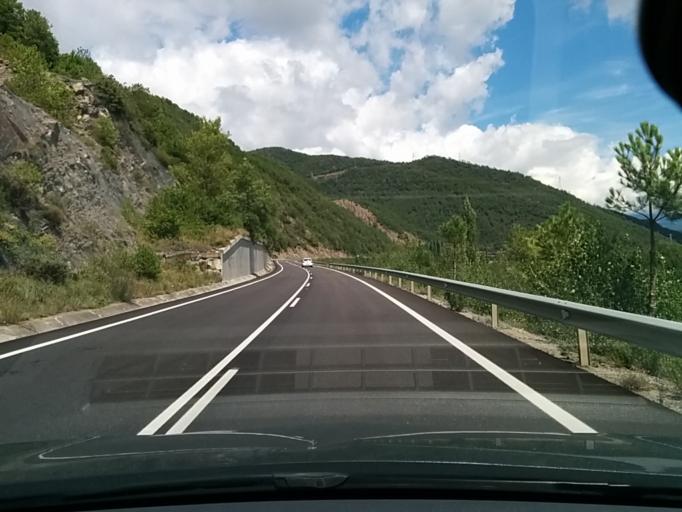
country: ES
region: Aragon
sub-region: Provincia de Huesca
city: Labuerda
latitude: 42.4562
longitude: 0.1367
